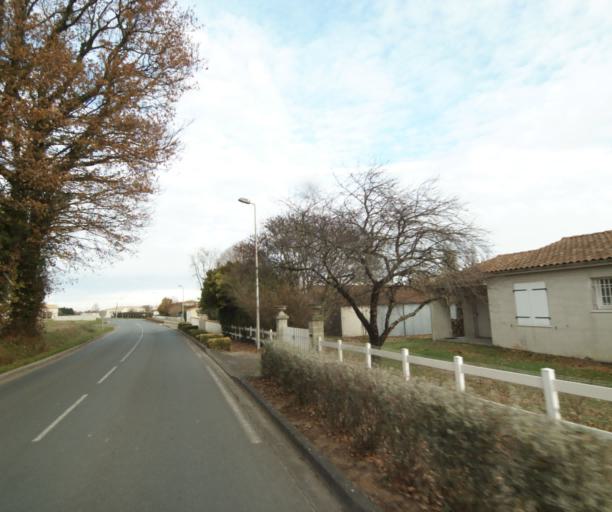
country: FR
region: Poitou-Charentes
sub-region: Departement de la Charente-Maritime
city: Corme-Royal
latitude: 45.7480
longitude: -0.8082
